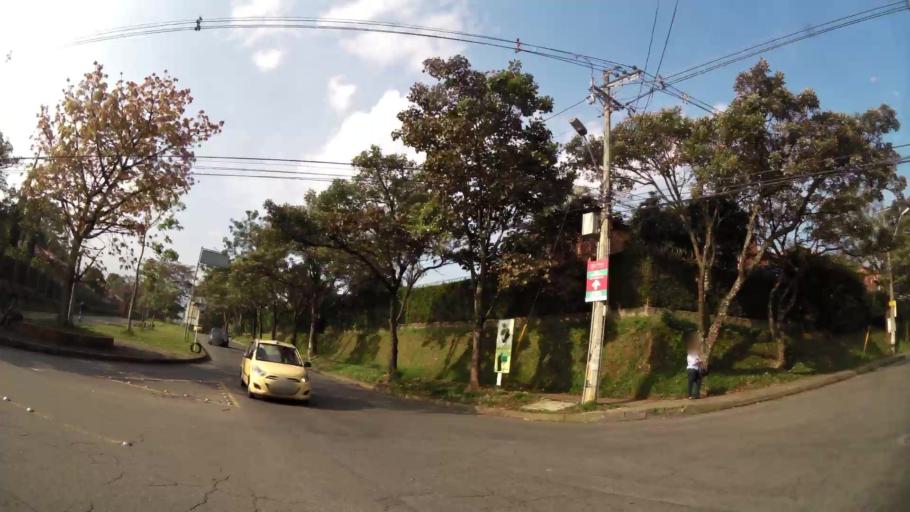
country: CO
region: Antioquia
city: Sabaneta
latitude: 6.1605
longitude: -75.6283
